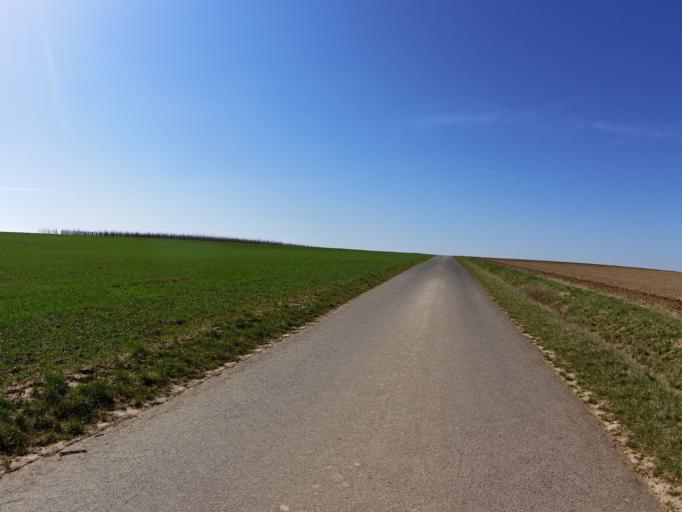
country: DE
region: Bavaria
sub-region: Regierungsbezirk Unterfranken
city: Prosselsheim
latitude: 49.8461
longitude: 10.1351
